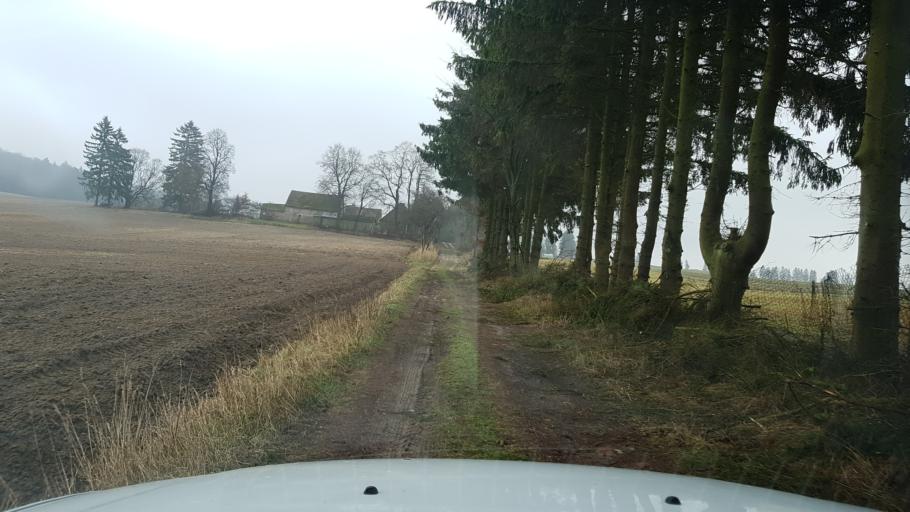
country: PL
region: West Pomeranian Voivodeship
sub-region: Powiat drawski
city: Czaplinek
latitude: 53.5786
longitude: 16.2592
